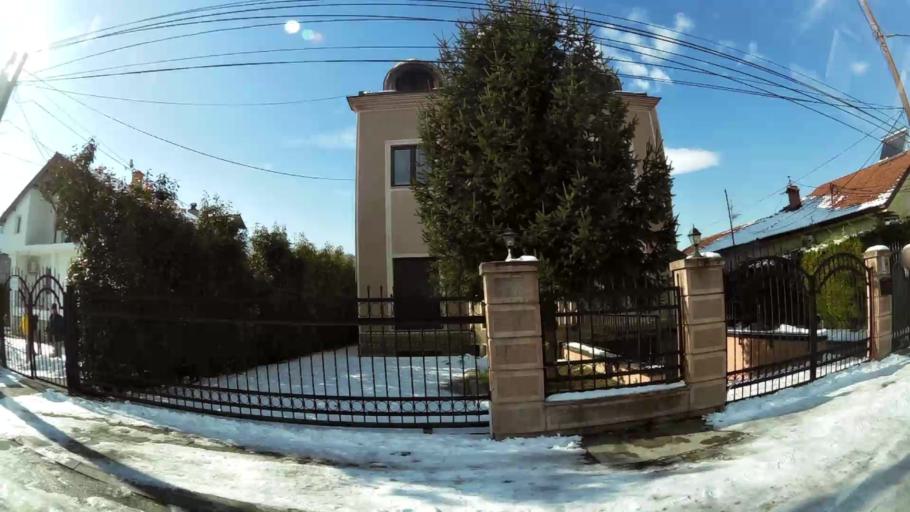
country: MK
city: Krushopek
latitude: 41.9994
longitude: 21.3705
